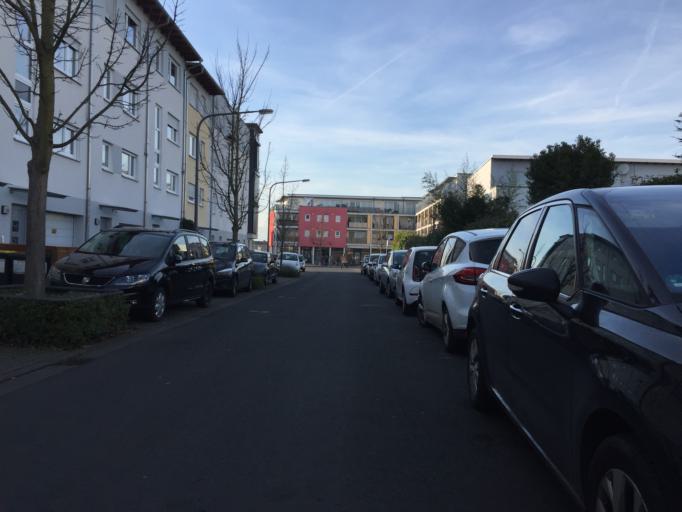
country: DE
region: Hesse
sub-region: Regierungsbezirk Darmstadt
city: Frankfurt am Main
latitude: 50.1622
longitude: 8.6636
